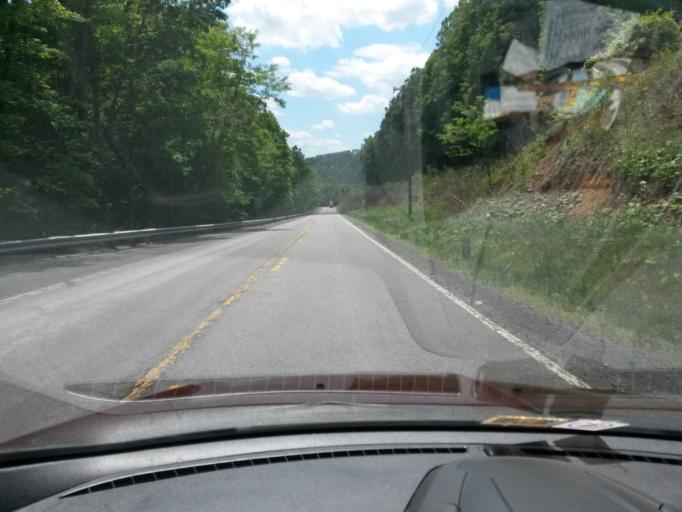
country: US
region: West Virginia
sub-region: Greenbrier County
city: Rainelle
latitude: 38.0096
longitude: -80.7290
